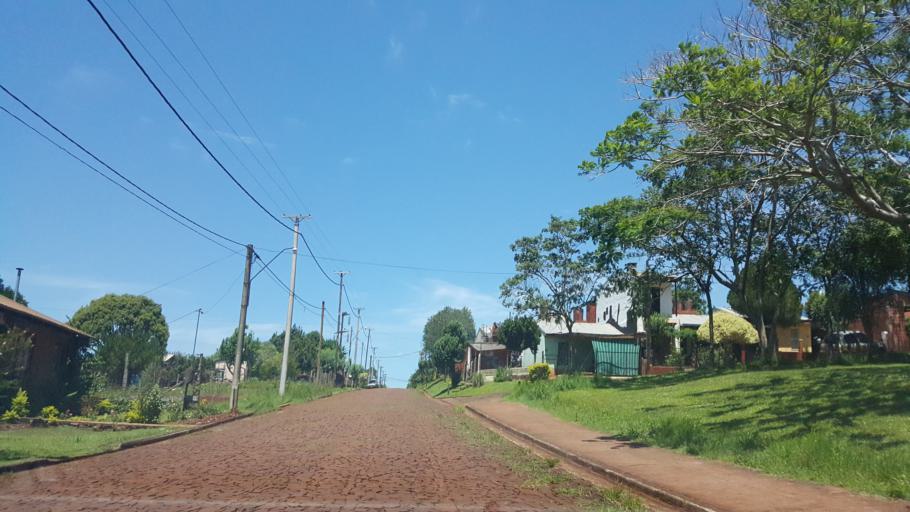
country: AR
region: Misiones
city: Capiovi
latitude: -26.9318
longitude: -55.0532
